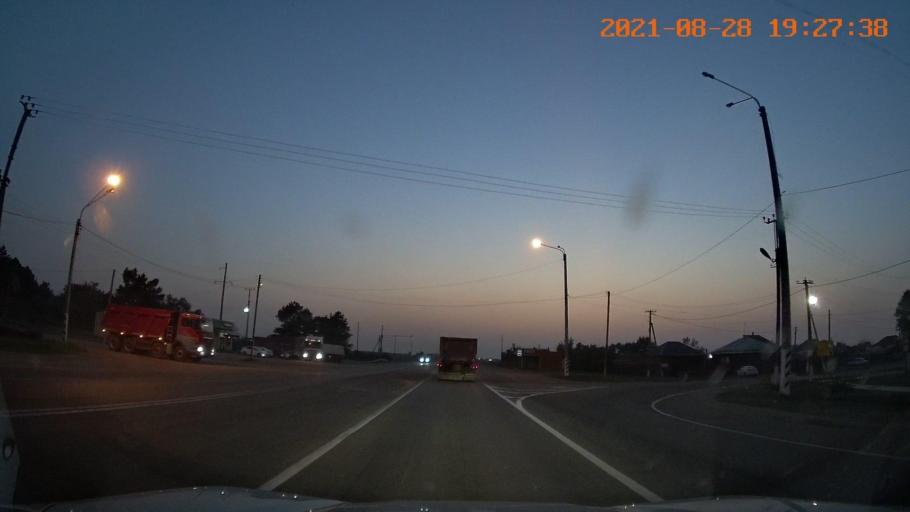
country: RU
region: Adygeya
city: Ponezhukay
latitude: 44.8787
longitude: 39.3815
